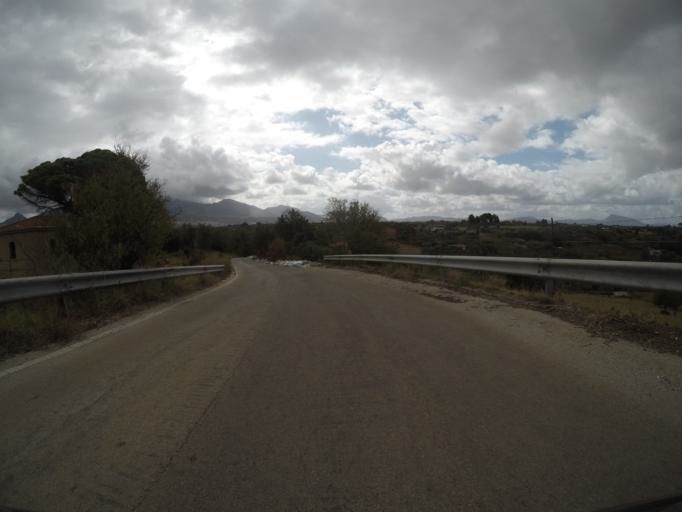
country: IT
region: Sicily
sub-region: Palermo
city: Partinico
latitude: 38.0834
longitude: 13.1083
